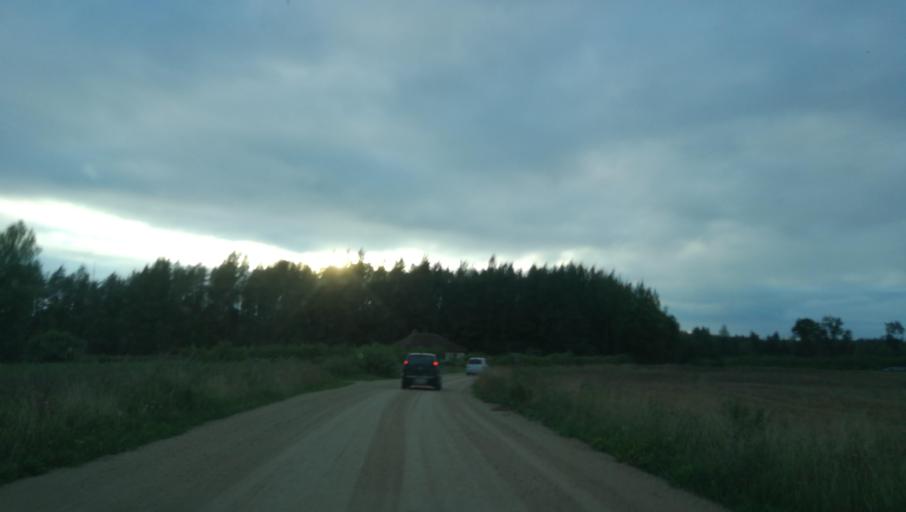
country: LV
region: Incukalns
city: Incukalns
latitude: 57.0274
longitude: 24.7963
